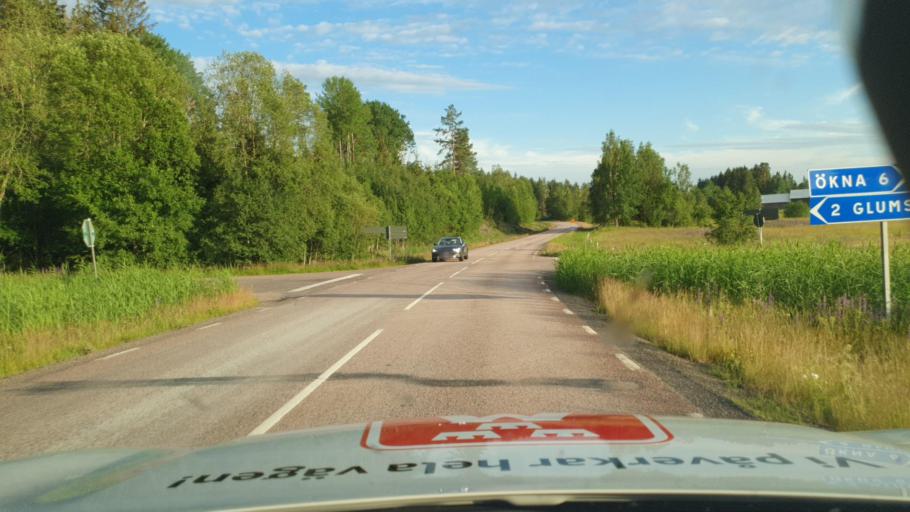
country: SE
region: Vaermland
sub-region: Karlstads Kommun
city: Molkom
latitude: 59.4913
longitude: 13.8041
